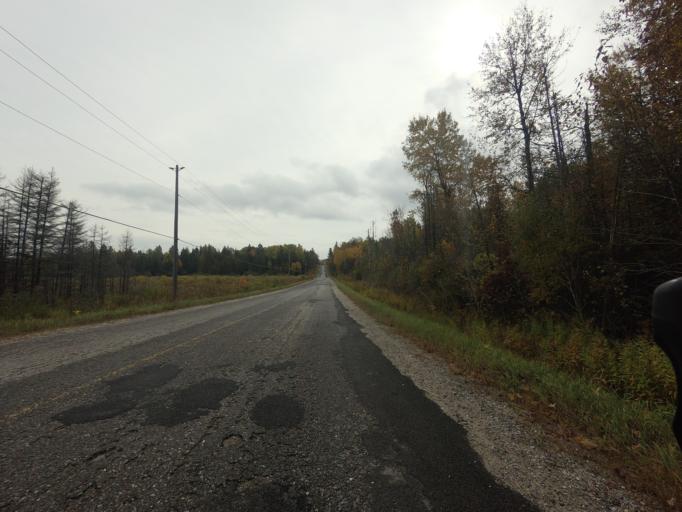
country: CA
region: Ontario
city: Perth
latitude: 45.1195
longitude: -76.5175
